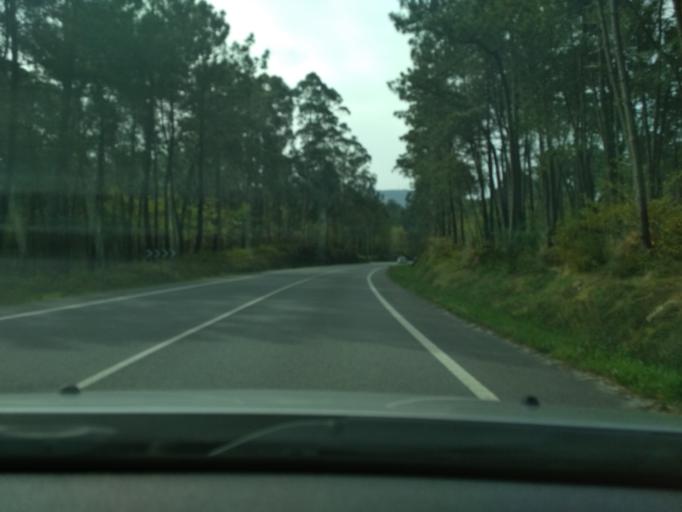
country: ES
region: Galicia
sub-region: Provincia de Pontevedra
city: Catoira
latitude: 42.6668
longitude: -8.7039
